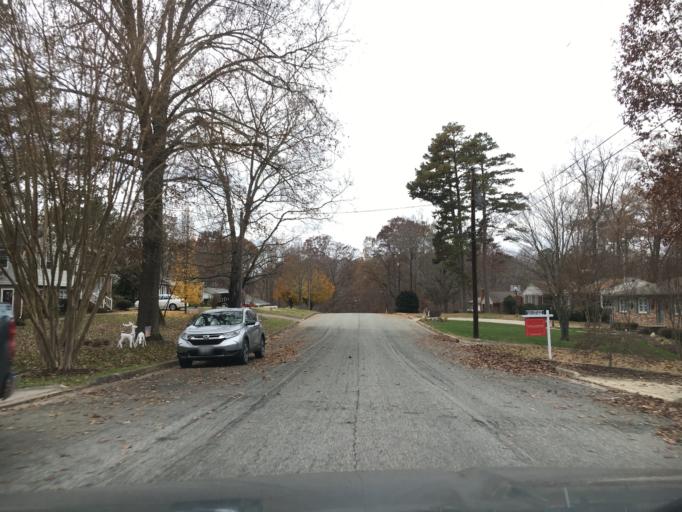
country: US
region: Virginia
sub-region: Halifax County
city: South Boston
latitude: 36.7280
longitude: -78.9103
